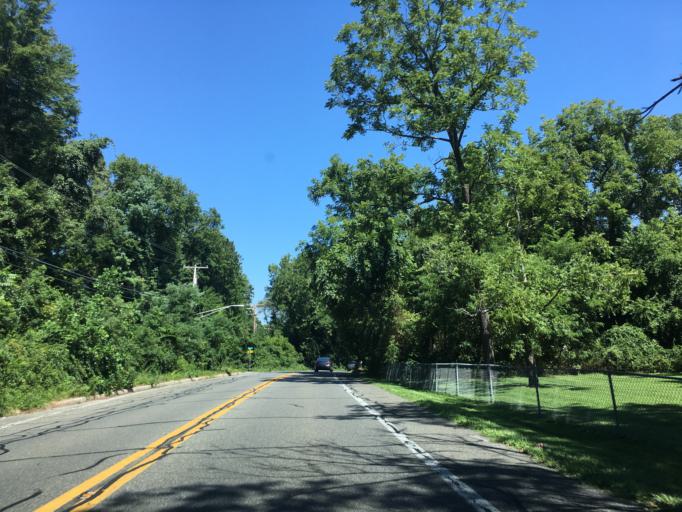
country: US
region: Maryland
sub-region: Anne Arundel County
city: Gambrills
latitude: 39.0607
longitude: -76.6288
